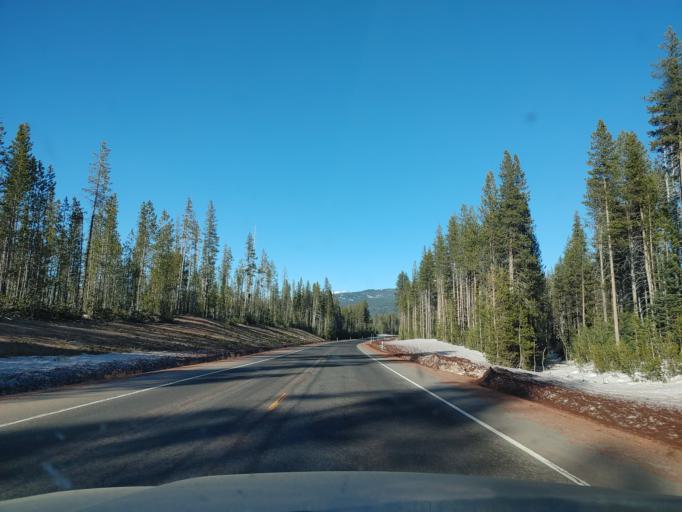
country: US
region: Oregon
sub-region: Lane County
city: Oakridge
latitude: 43.1155
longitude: -122.1676
